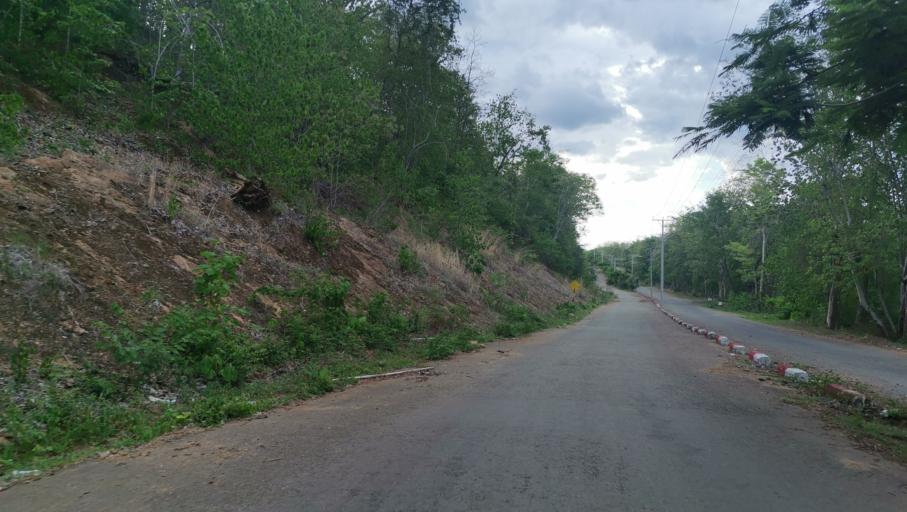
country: MM
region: Magway
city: Minbu
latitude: 20.0885
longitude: 94.5690
